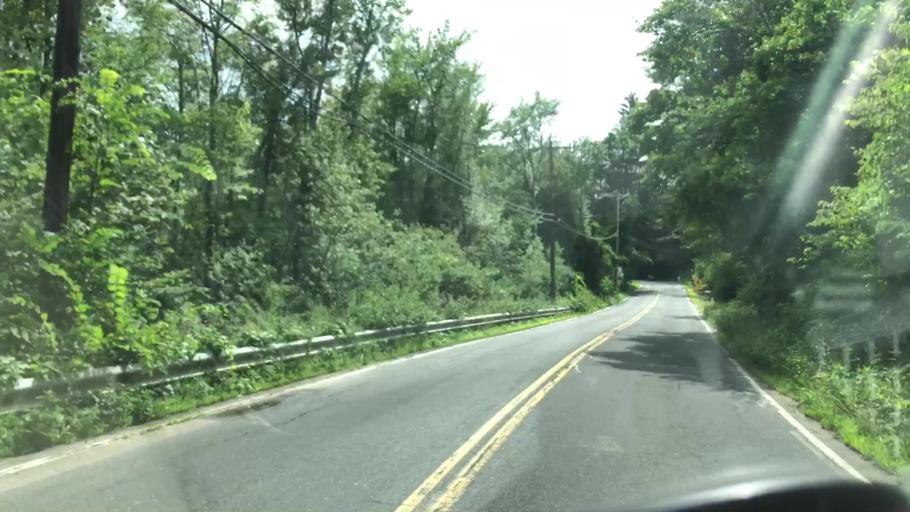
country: US
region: Massachusetts
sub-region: Hampden County
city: Holyoke
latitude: 42.2210
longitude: -72.6559
